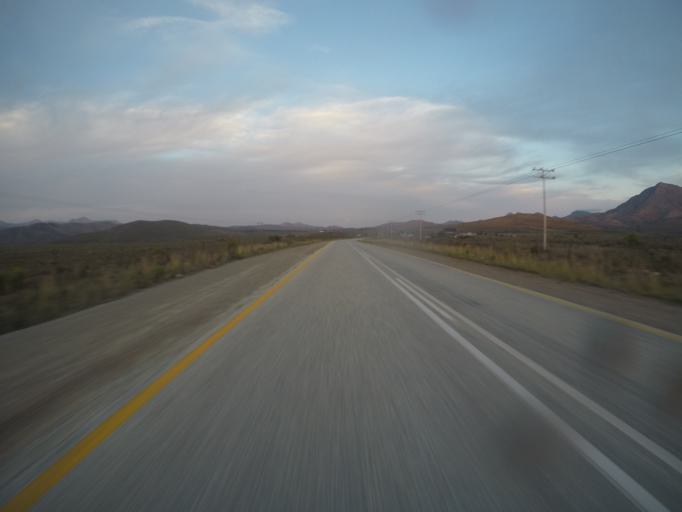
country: ZA
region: Western Cape
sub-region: Eden District Municipality
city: Plettenberg Bay
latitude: -33.7303
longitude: 23.3952
